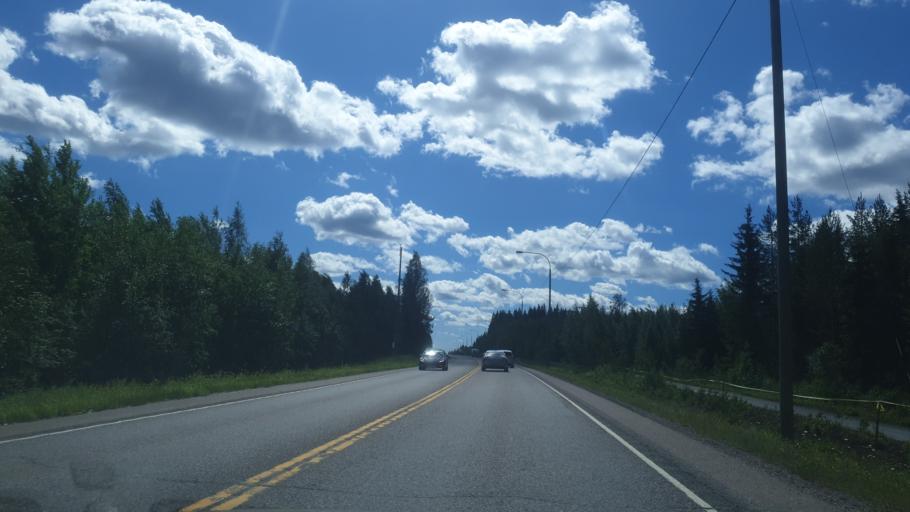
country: FI
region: Northern Savo
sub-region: Varkaus
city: Varkaus
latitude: 62.3844
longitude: 27.8095
